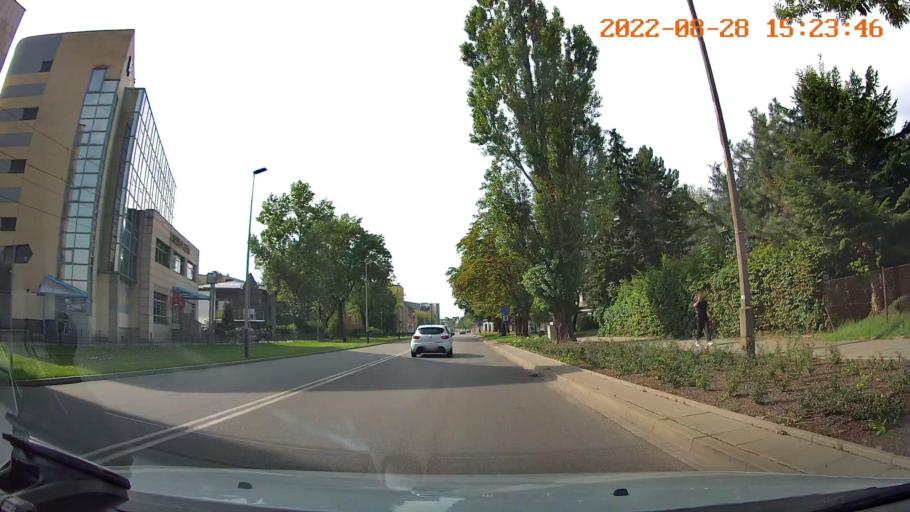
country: PL
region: Lesser Poland Voivodeship
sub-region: Krakow
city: Krakow
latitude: 50.0781
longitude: 19.9002
